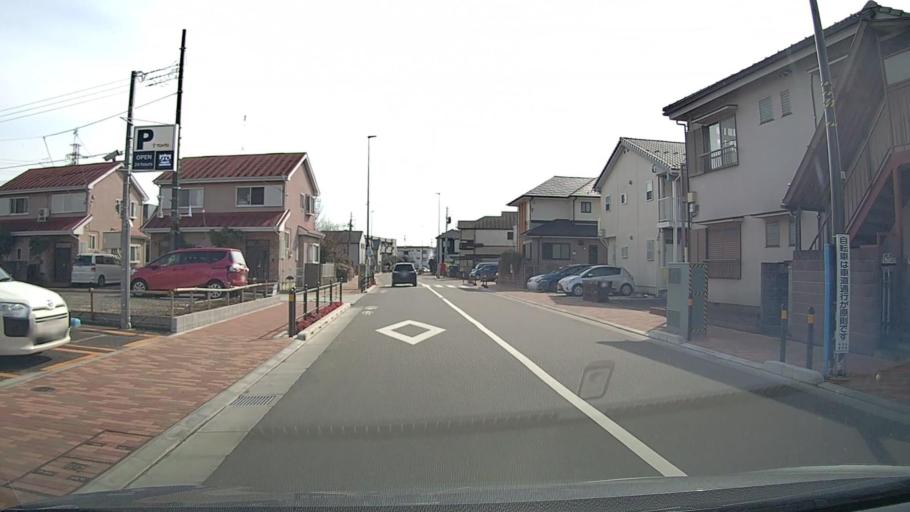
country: JP
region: Tokyo
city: Tanashicho
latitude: 35.7599
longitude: 139.5664
